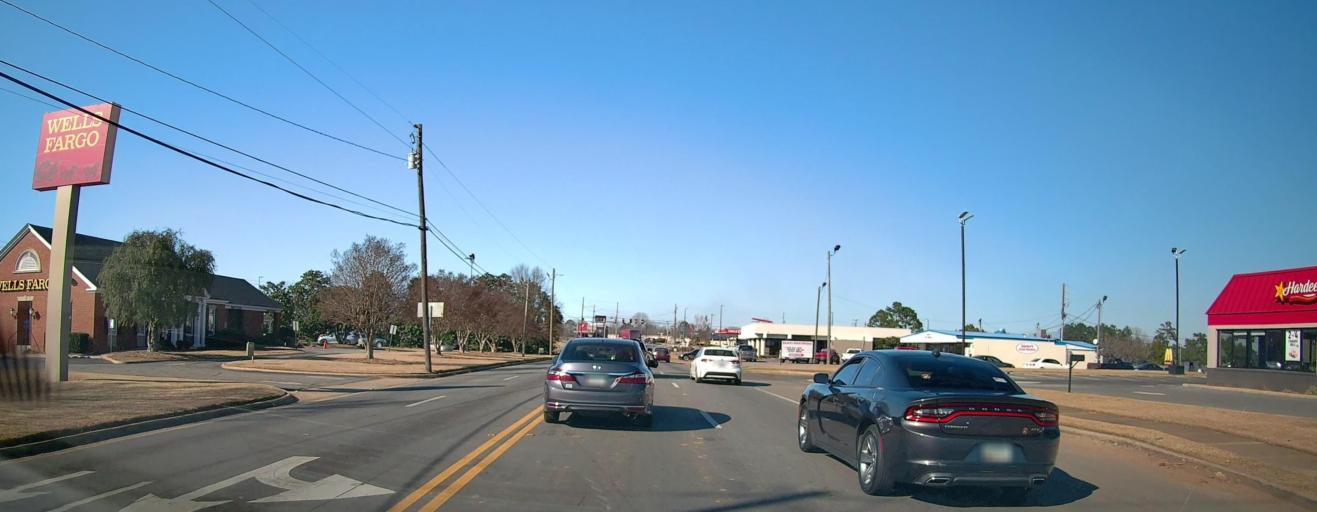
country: US
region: Georgia
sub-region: Sumter County
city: Americus
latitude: 32.0714
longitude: -84.2175
